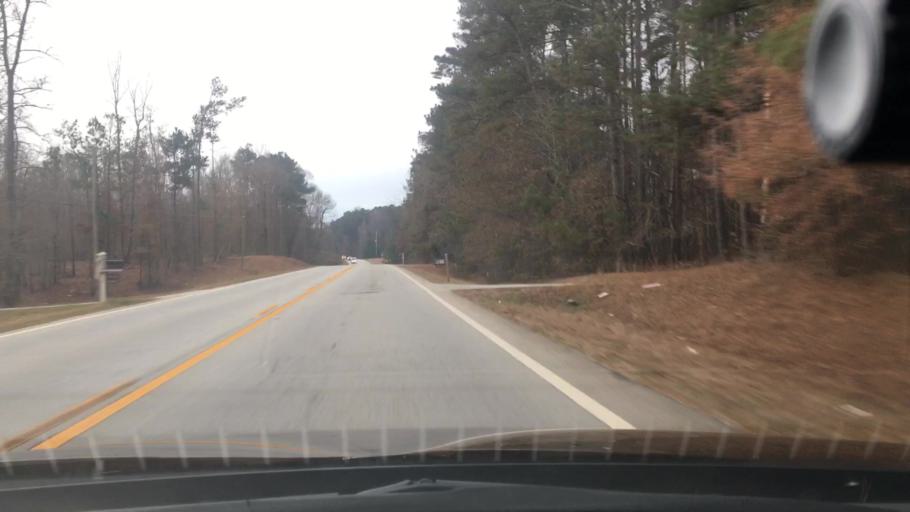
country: US
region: Georgia
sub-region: Fayette County
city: Peachtree City
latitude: 33.3524
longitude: -84.6386
